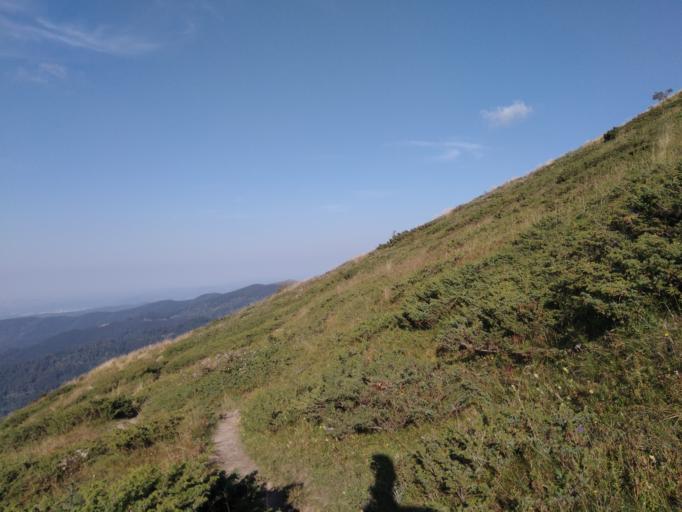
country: BG
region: Stara Zagora
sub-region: Obshtina Pavel Banya
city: Asen
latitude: 42.7621
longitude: 25.1058
